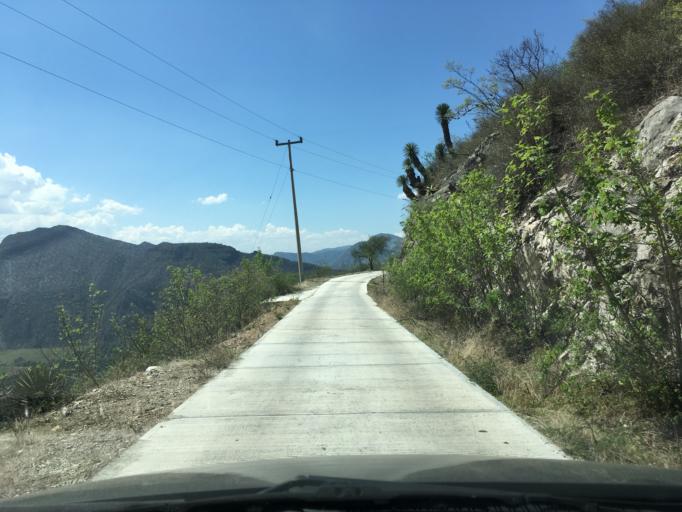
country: MX
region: Hidalgo
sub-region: Metztitlan
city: Fontezuelas
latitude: 20.6361
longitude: -98.8420
